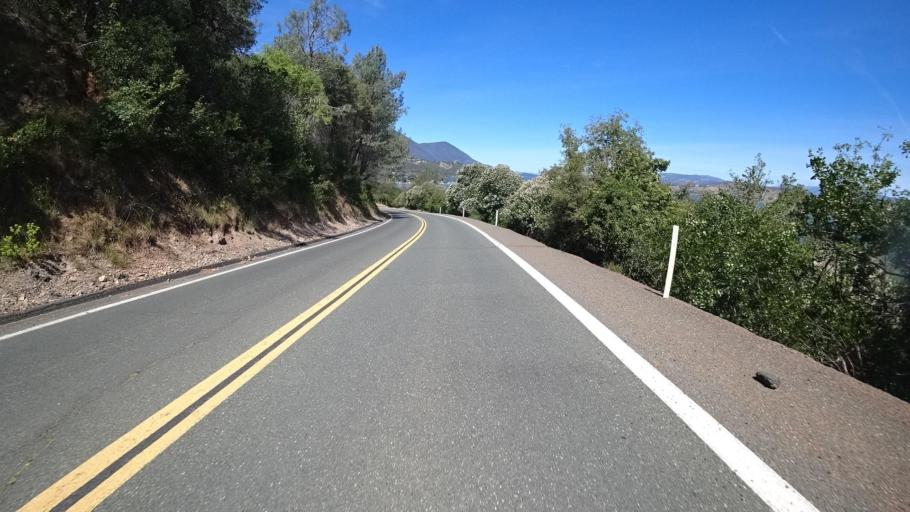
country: US
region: California
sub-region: Lake County
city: Clearlake
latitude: 38.9433
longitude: -122.6730
